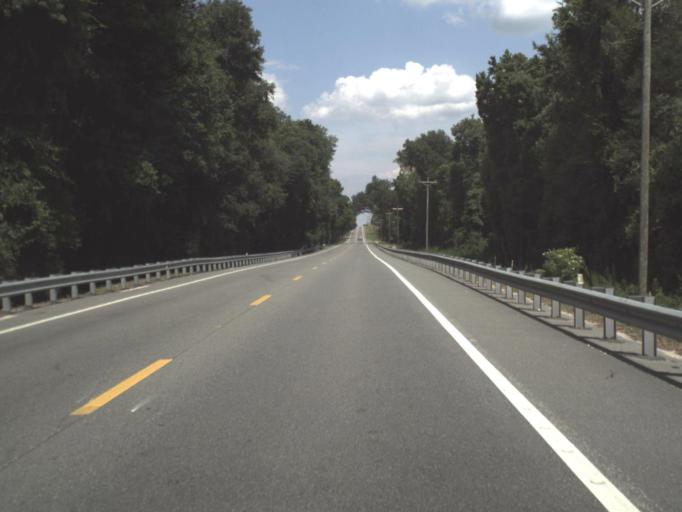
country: US
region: Florida
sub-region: Putnam County
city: Interlachen
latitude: 29.7319
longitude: -81.8654
